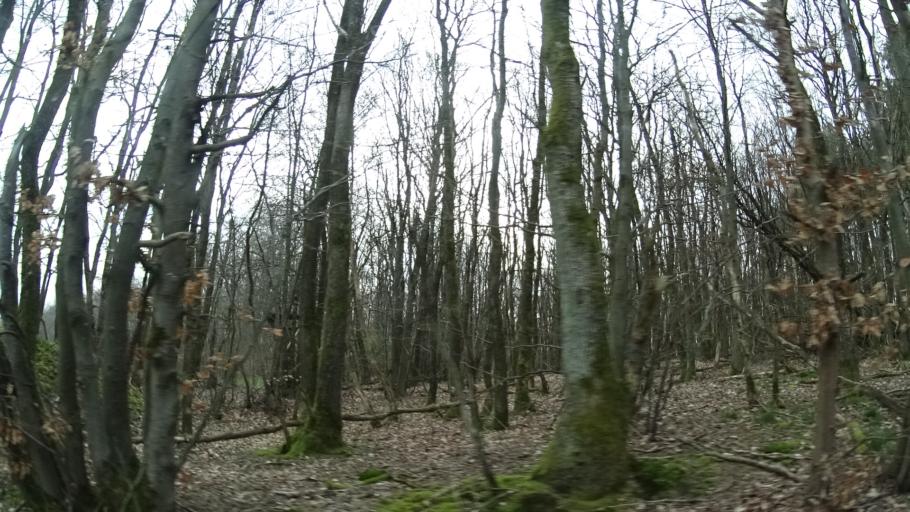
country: DE
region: Rheinland-Pfalz
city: Leisel
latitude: 49.7233
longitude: 7.2175
